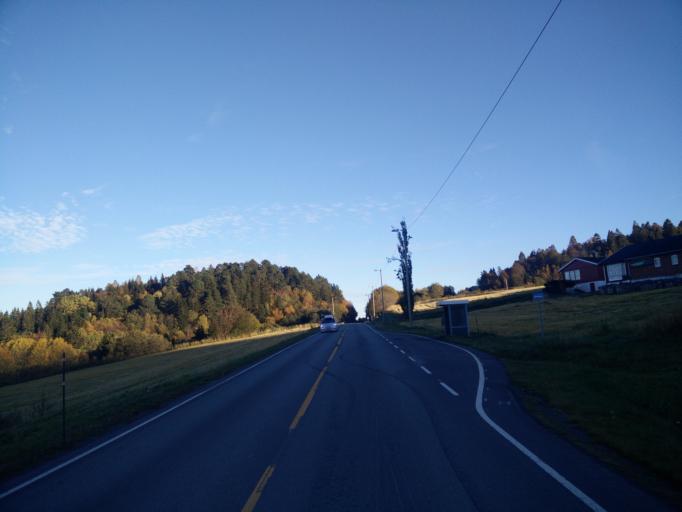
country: NO
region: Sor-Trondelag
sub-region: Skaun
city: Borsa
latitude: 63.3465
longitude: 10.0375
